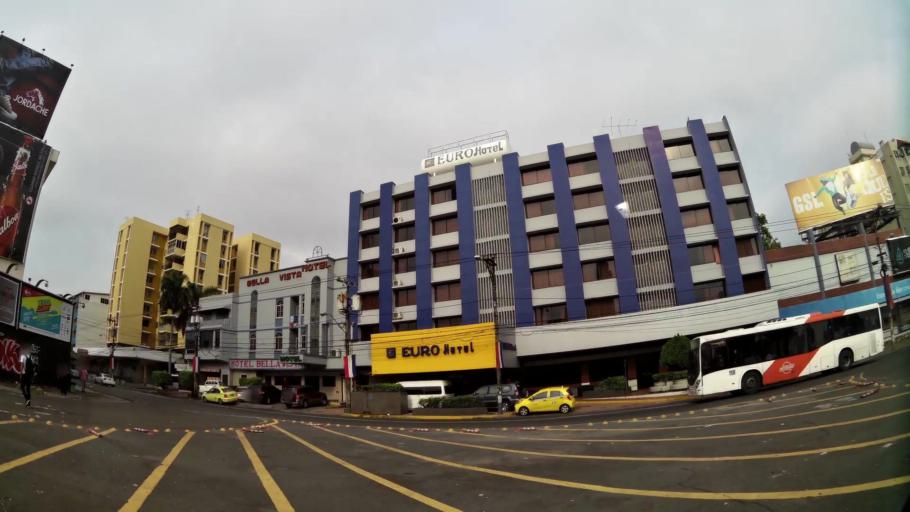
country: PA
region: Panama
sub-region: Distrito de Panama
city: Ancon
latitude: 8.9750
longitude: -79.5345
